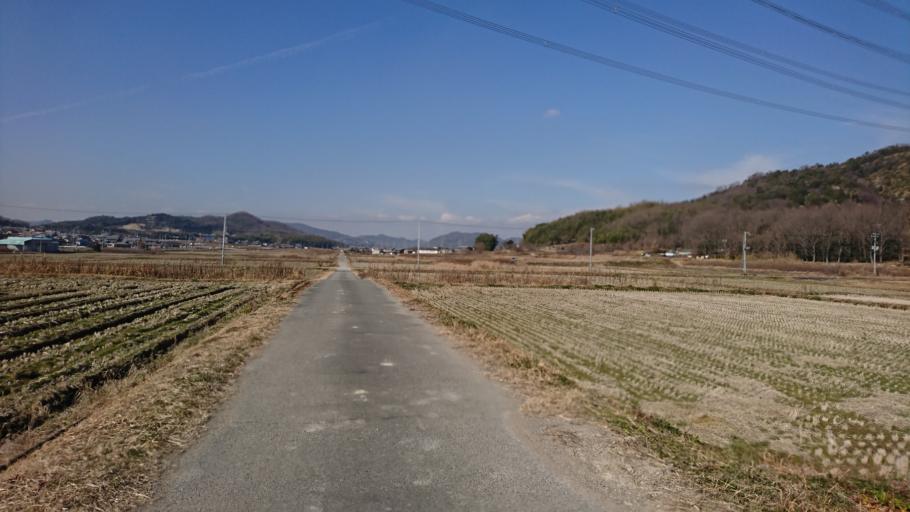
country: JP
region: Hyogo
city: Kakogawacho-honmachi
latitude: 34.8113
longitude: 134.8603
